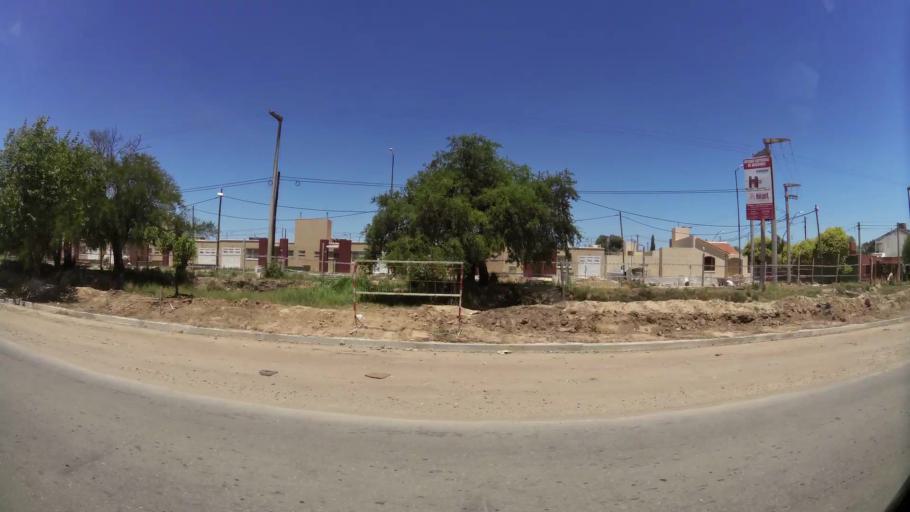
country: AR
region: Cordoba
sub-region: Departamento de Capital
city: Cordoba
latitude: -31.3771
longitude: -64.1308
